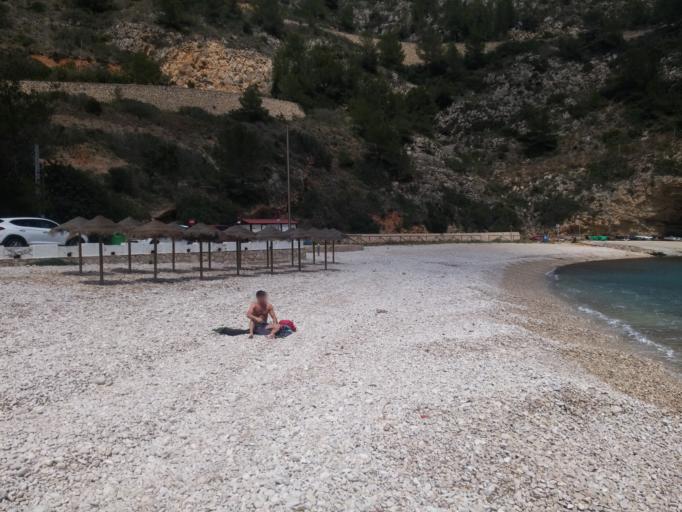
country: ES
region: Valencia
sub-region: Provincia de Alicante
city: Benitachell
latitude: 38.7294
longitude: 0.1966
